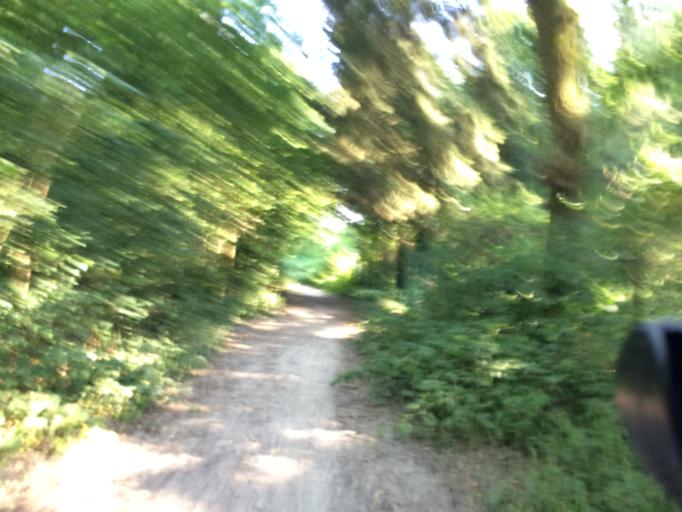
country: FR
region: Ile-de-France
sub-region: Departement de l'Essonne
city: Soisy-sur-Seine
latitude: 48.6552
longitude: 2.4671
